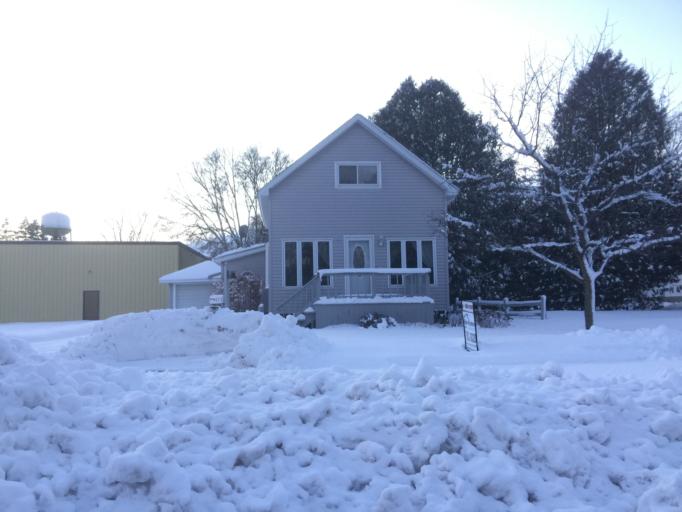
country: US
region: Wisconsin
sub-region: Marinette County
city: Peshtigo
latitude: 45.0475
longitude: -87.7487
